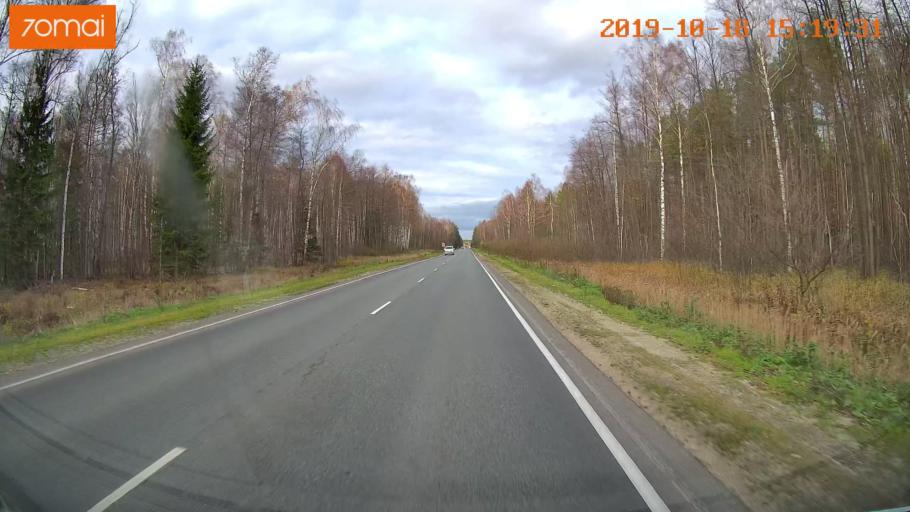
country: RU
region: Vladimir
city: Anopino
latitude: 55.6743
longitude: 40.7383
